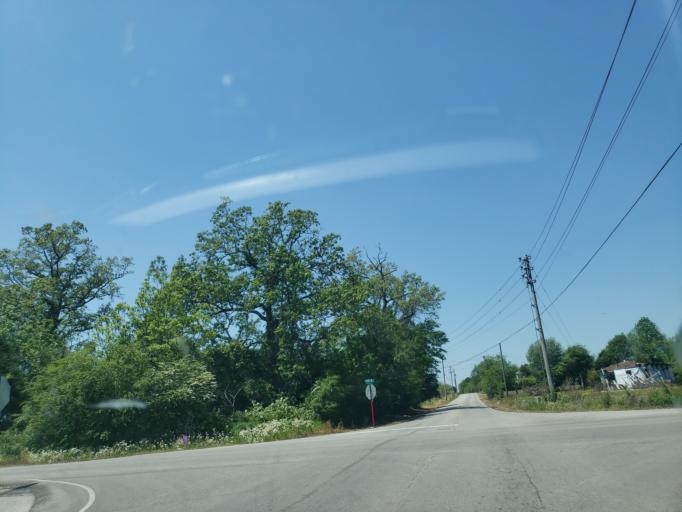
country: US
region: Alabama
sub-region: Madison County
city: Hazel Green
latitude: 34.9624
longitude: -86.6773
